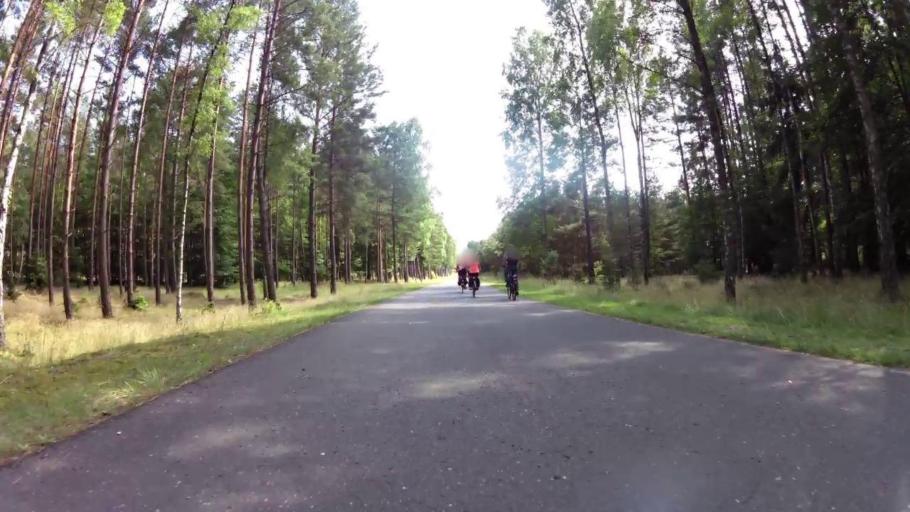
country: PL
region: West Pomeranian Voivodeship
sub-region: Powiat choszczenski
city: Drawno
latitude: 53.3498
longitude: 15.7028
